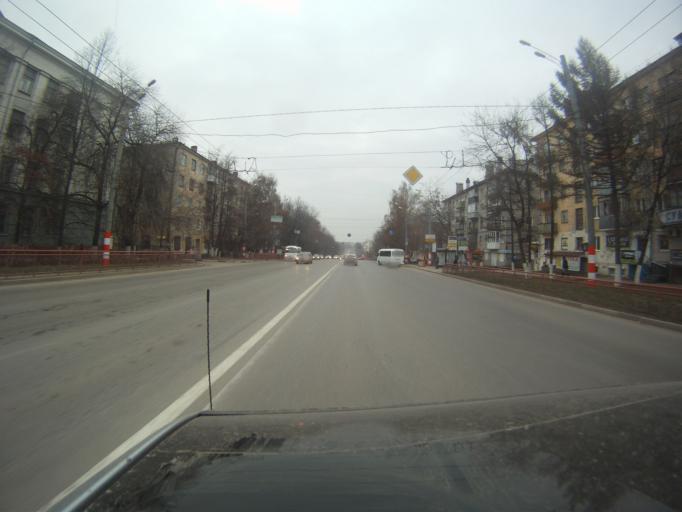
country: RU
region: Nizjnij Novgorod
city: Nizhniy Novgorod
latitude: 56.2914
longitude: 43.9841
